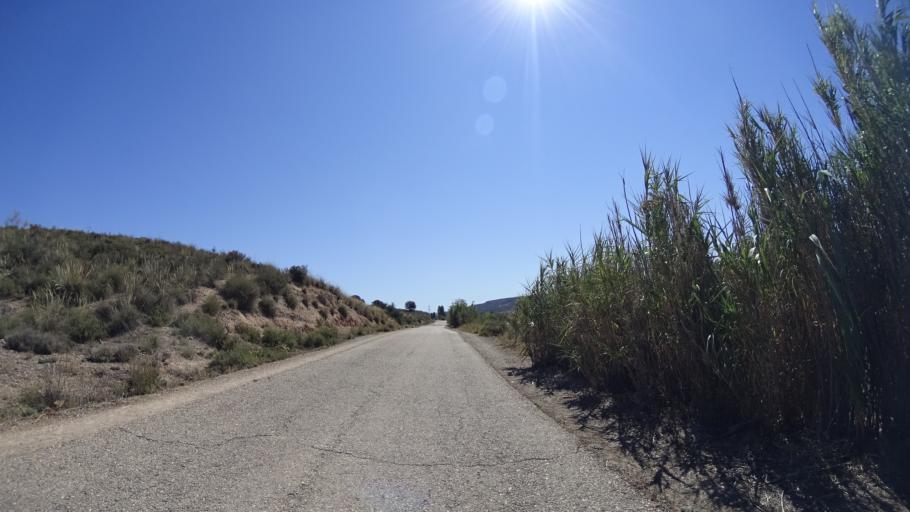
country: ES
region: Madrid
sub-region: Provincia de Madrid
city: Morata de Tajuna
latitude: 40.2297
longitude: -3.4207
